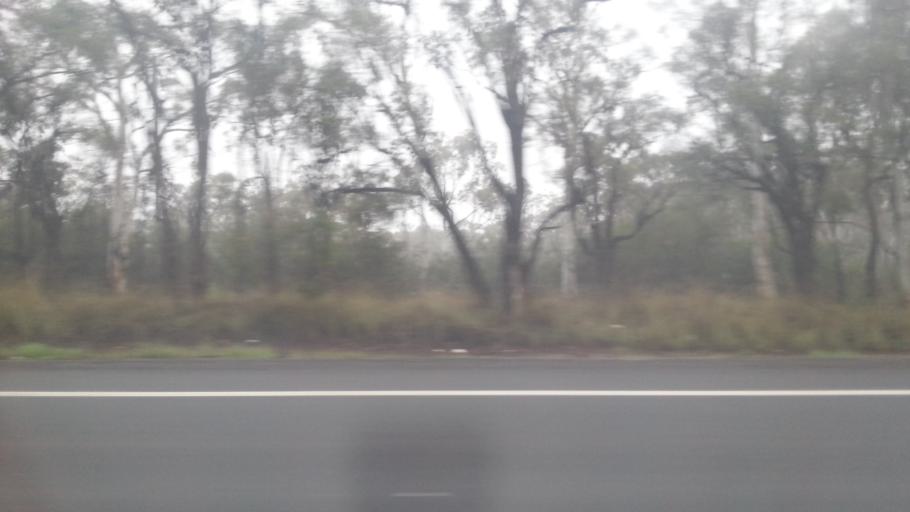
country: AU
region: New South Wales
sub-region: Hawkesbury
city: South Windsor
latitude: -33.6565
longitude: 150.7702
